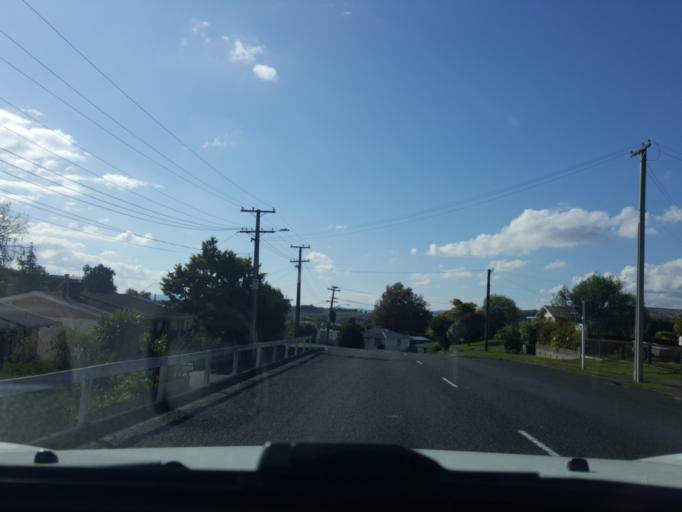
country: NZ
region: Waikato
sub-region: Waikato District
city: Ngaruawahia
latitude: -37.5429
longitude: 175.1701
